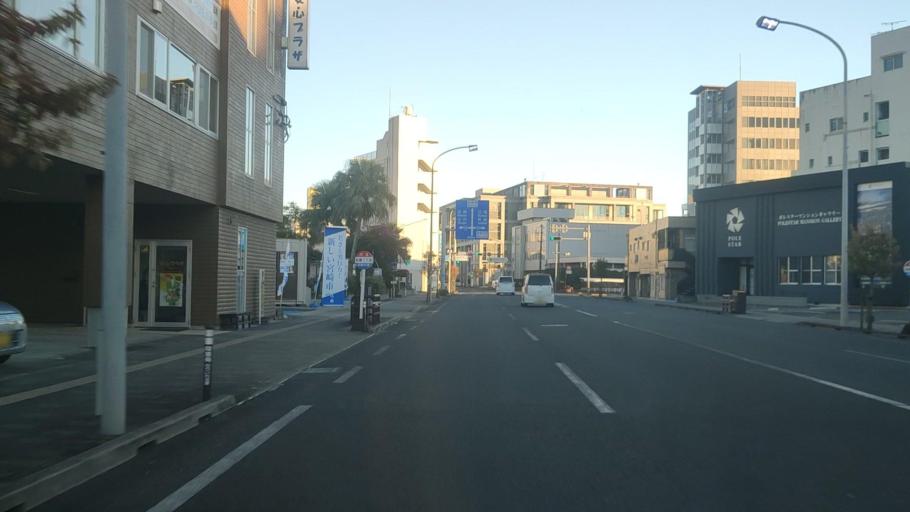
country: JP
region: Miyazaki
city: Miyazaki-shi
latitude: 31.9096
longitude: 131.4184
